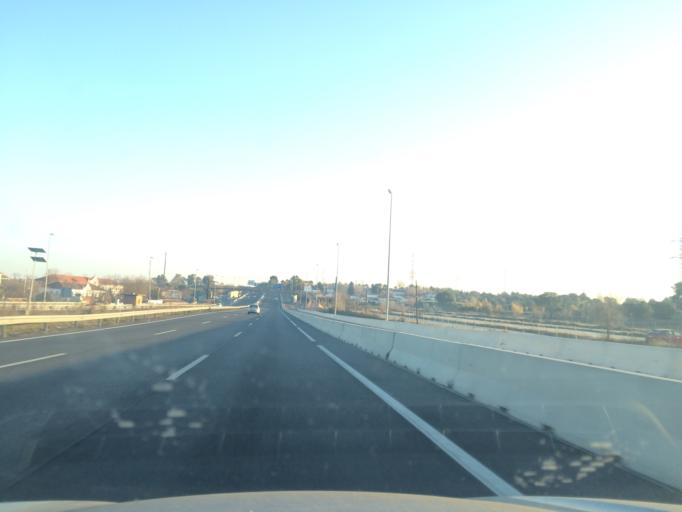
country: ES
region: Madrid
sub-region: Provincia de Madrid
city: Tres Cantos
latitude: 40.5580
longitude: -3.7121
